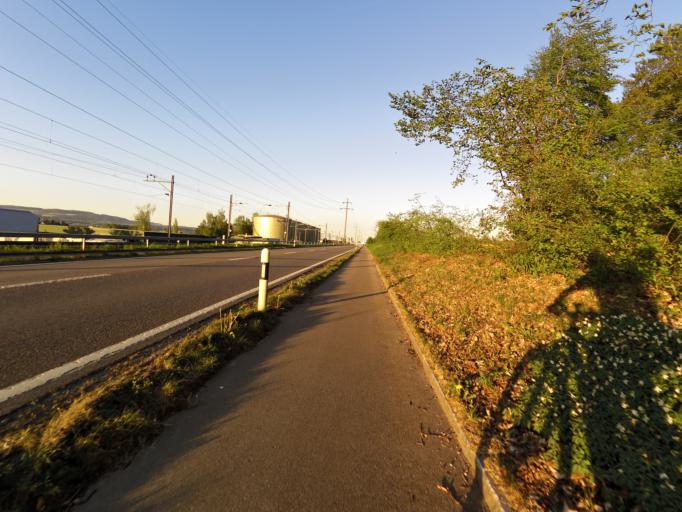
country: CH
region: Thurgau
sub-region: Frauenfeld District
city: Gachnang
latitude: 47.5496
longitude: 8.8535
